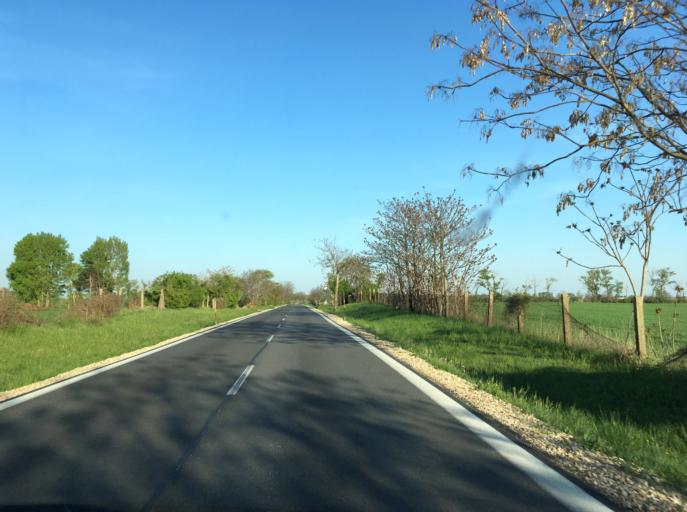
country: AT
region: Burgenland
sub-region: Politischer Bezirk Neusiedl am See
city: Deutsch Jahrndorf
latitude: 48.0632
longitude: 17.1207
